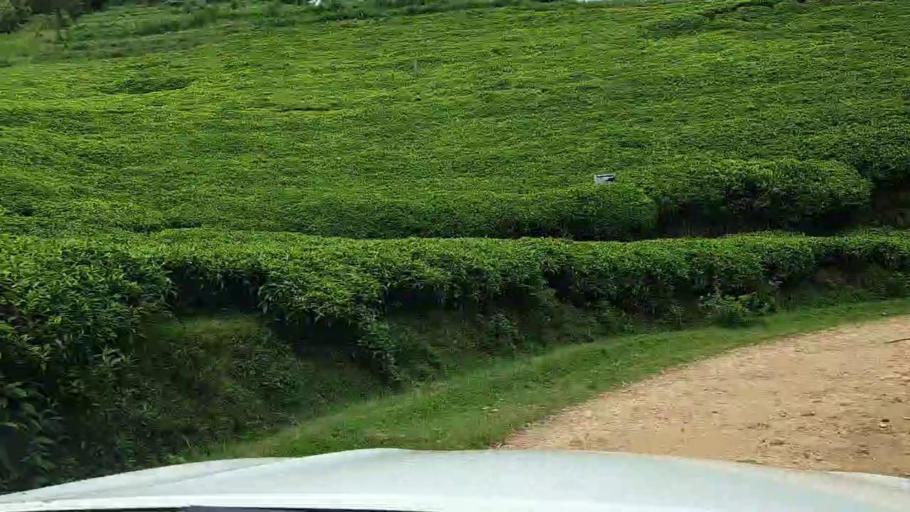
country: RW
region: Western Province
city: Kibuye
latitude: -2.2881
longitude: 29.3748
